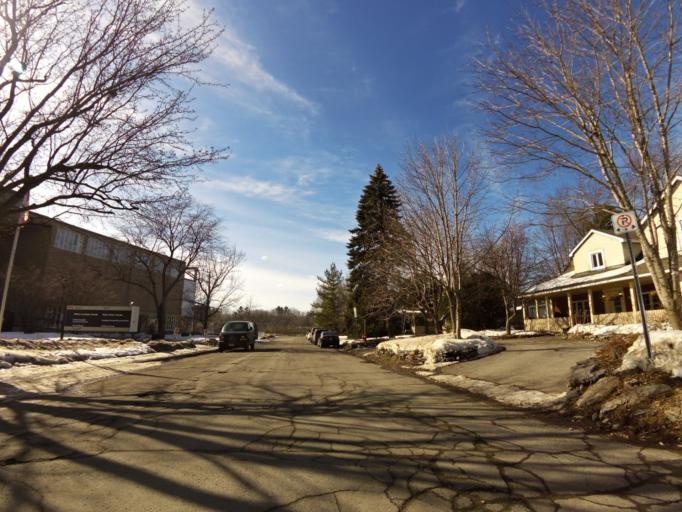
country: CA
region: Ontario
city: Ottawa
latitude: 45.4359
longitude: -75.7449
